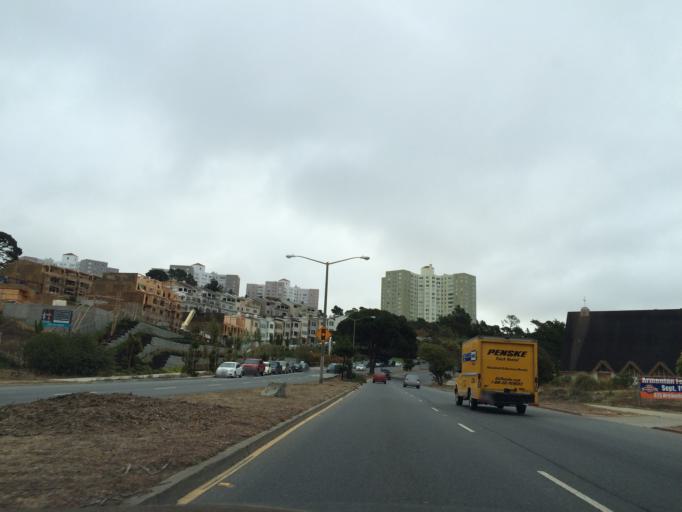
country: US
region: California
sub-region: San Mateo County
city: Daly City
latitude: 37.7145
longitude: -122.4784
